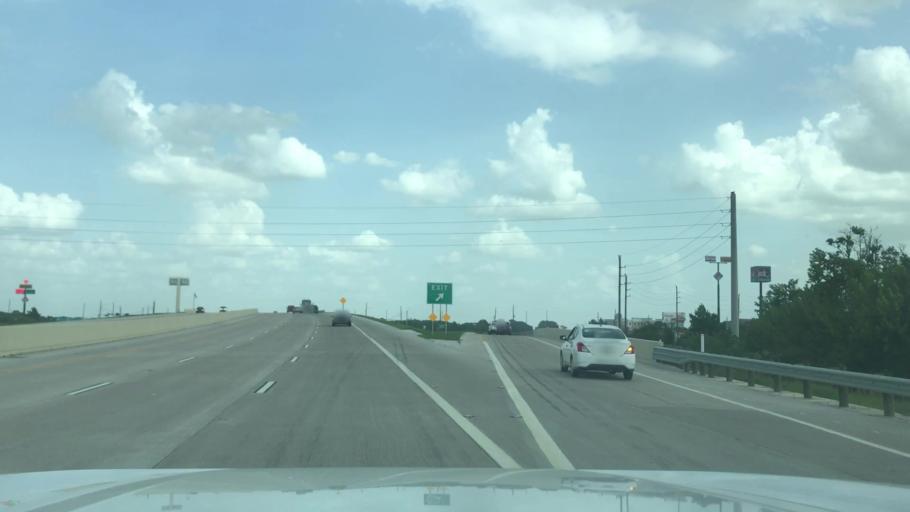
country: US
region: Texas
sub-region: Waller County
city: Waller
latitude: 30.0647
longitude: -95.9128
